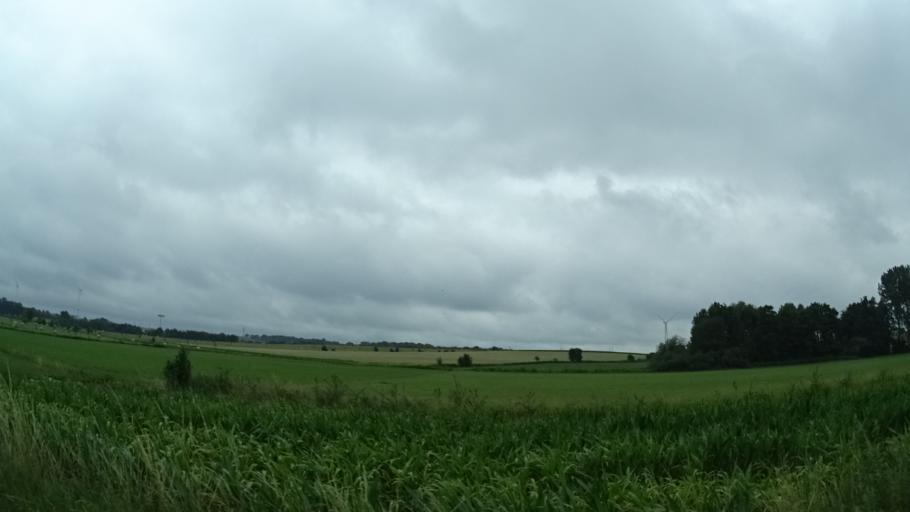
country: LU
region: Luxembourg
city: Eischen
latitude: 49.6492
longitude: 5.8796
